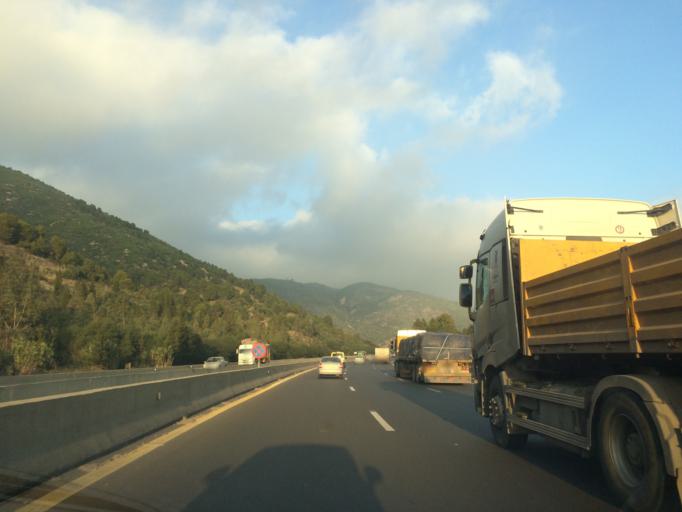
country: DZ
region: Tipaza
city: Hadjout
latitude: 36.3873
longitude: 2.4937
